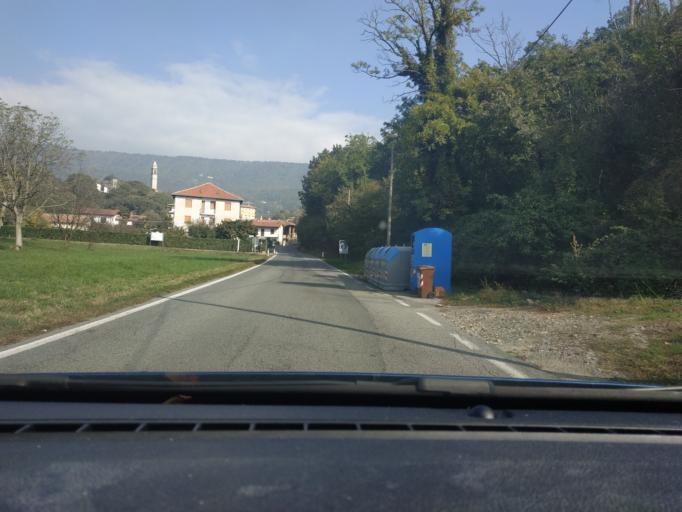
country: IT
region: Piedmont
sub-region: Provincia di Torino
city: Chiaverano
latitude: 45.4913
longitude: 7.9011
